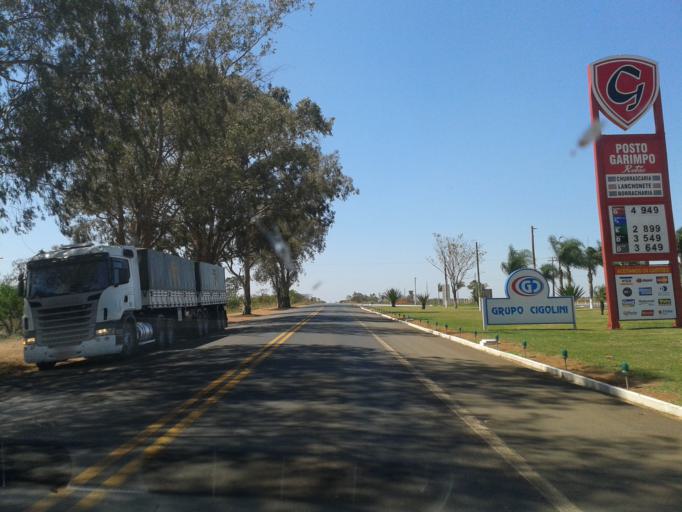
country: BR
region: Minas Gerais
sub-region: Uberaba
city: Uberaba
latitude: -19.3146
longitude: -47.5716
